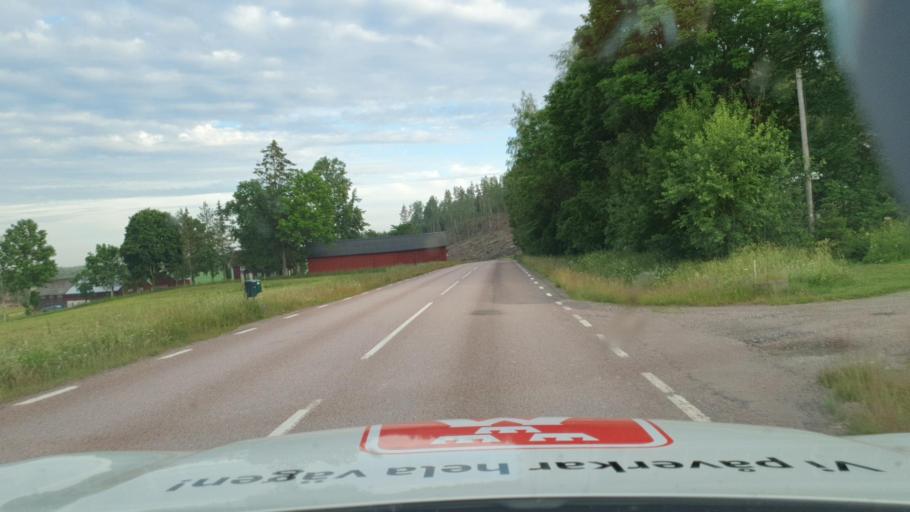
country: SE
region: Vaermland
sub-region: Karlstads Kommun
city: Molkom
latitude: 59.5563
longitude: 13.7792
